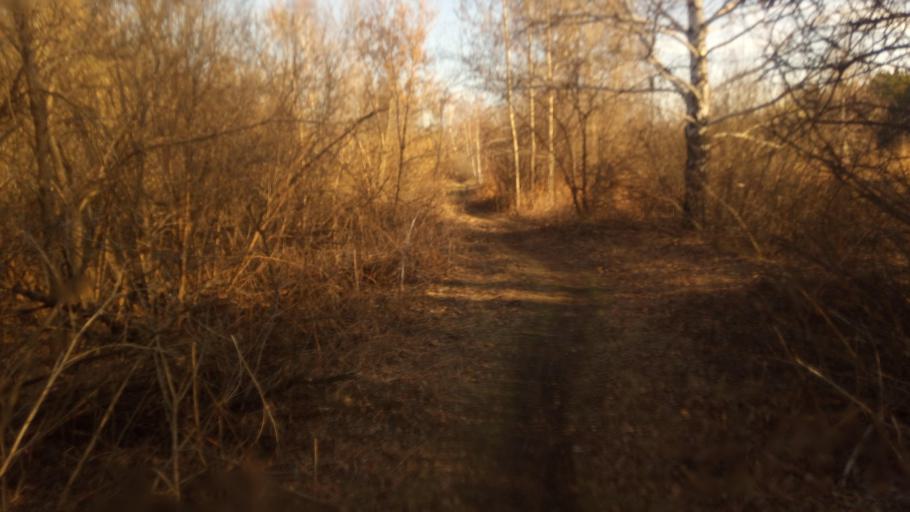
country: RU
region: Chelyabinsk
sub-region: Gorod Chelyabinsk
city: Chelyabinsk
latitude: 55.1512
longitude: 61.3236
